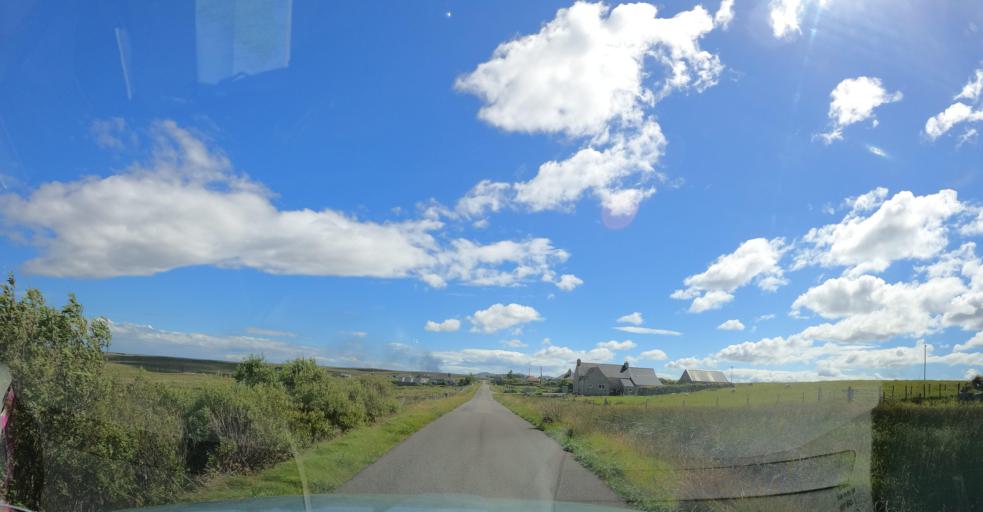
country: GB
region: Scotland
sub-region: Eilean Siar
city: Isle of Lewis
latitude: 58.3527
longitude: -6.5474
